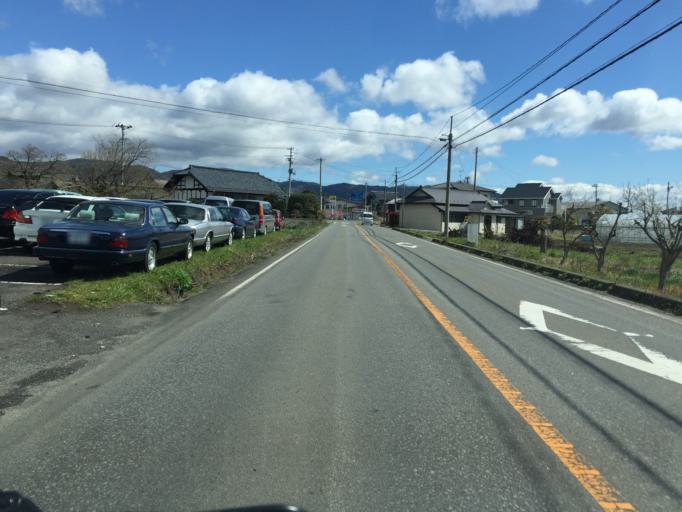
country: JP
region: Fukushima
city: Fukushima-shi
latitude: 37.8171
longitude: 140.4339
